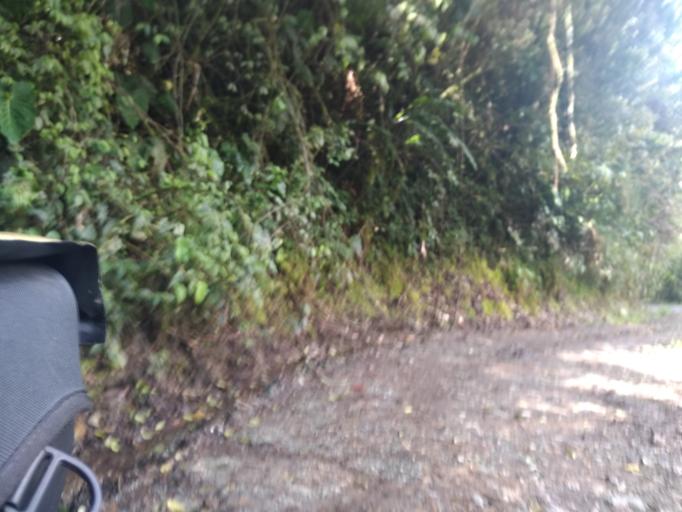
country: EC
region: Tungurahua
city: Banos
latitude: -1.4047
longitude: -78.2781
